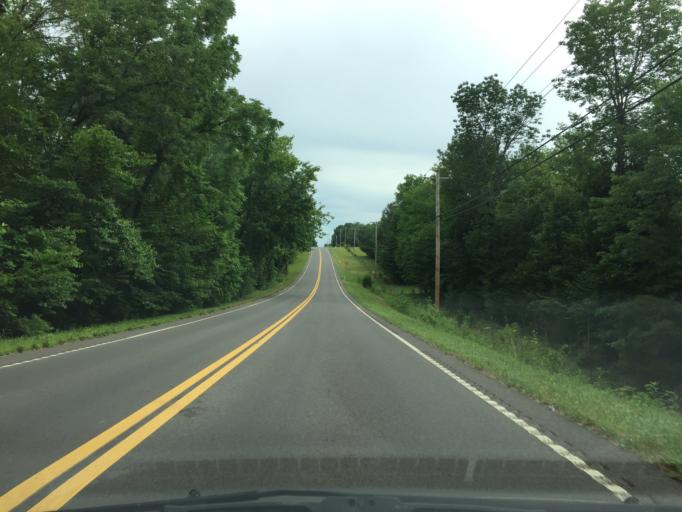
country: US
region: Tennessee
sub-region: Bradley County
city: Hopewell
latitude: 35.3190
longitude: -84.9438
